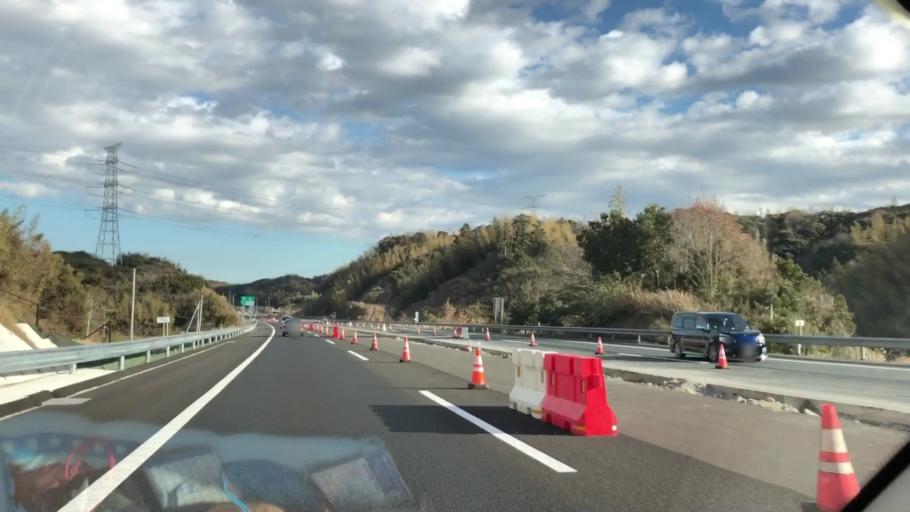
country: JP
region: Chiba
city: Kimitsu
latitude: 35.2782
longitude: 139.9232
